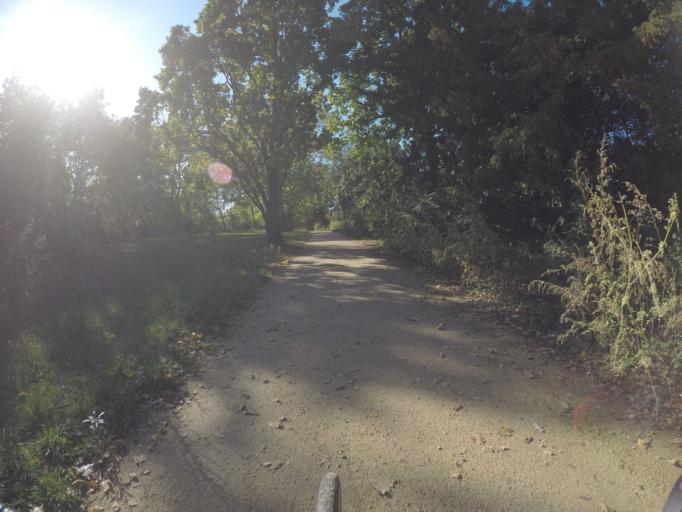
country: DE
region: Berlin
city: Charlottenburg Bezirk
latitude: 52.5252
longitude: 13.2855
